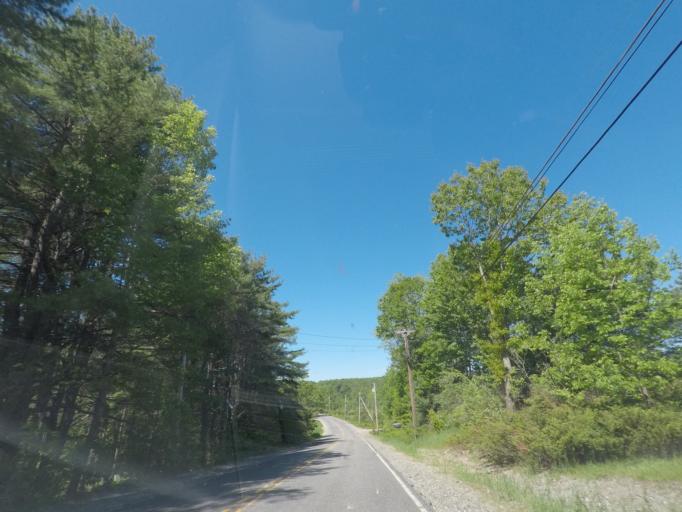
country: US
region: Maine
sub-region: Kennebec County
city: Gardiner
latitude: 44.2290
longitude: -69.8691
